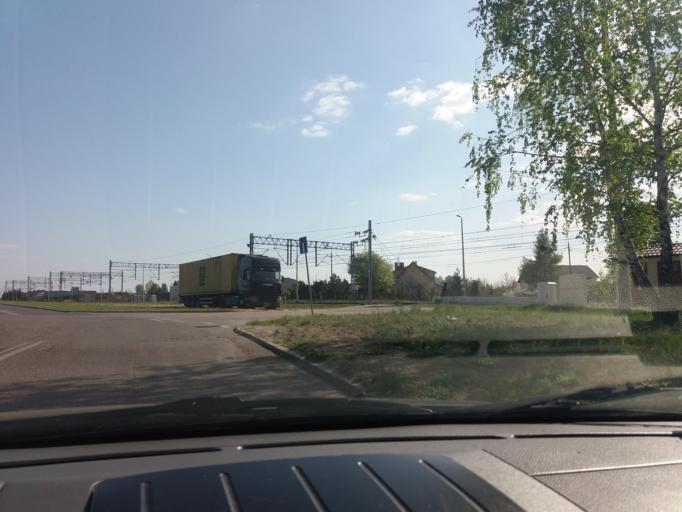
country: PL
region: Masovian Voivodeship
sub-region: Powiat mlawski
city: Mlawa
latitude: 53.1164
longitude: 20.3590
